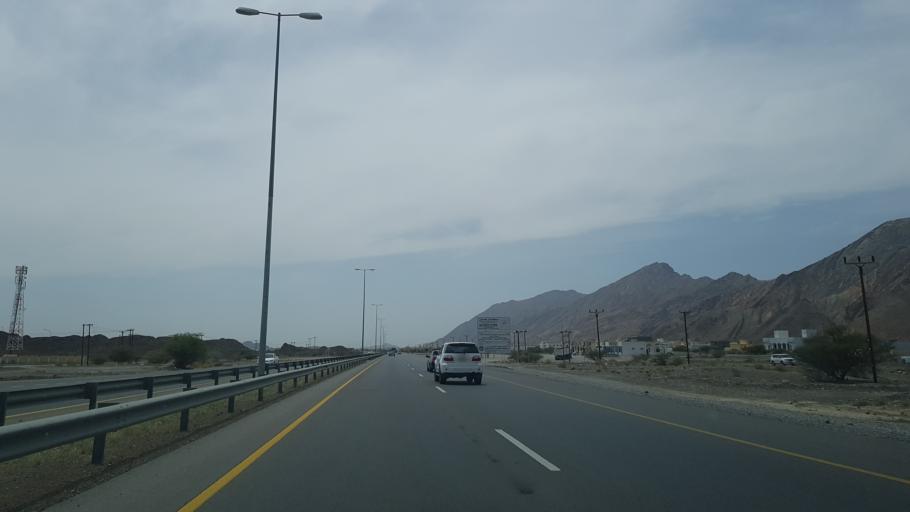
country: OM
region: Muhafazat ad Dakhiliyah
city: Izki
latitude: 23.0315
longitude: 57.7984
